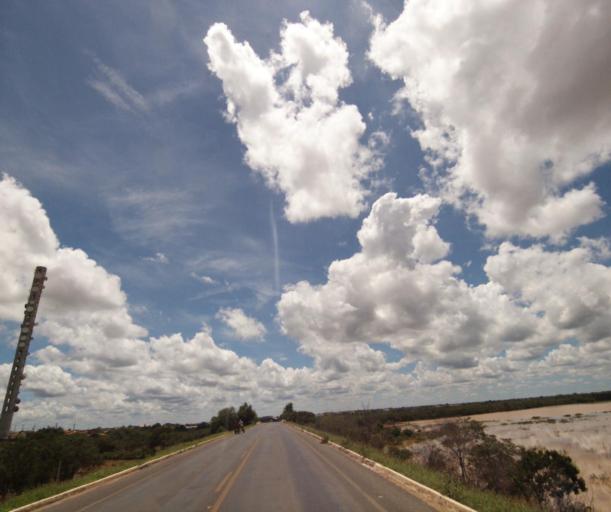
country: BR
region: Bahia
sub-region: Bom Jesus Da Lapa
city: Bom Jesus da Lapa
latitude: -13.2616
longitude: -43.4225
